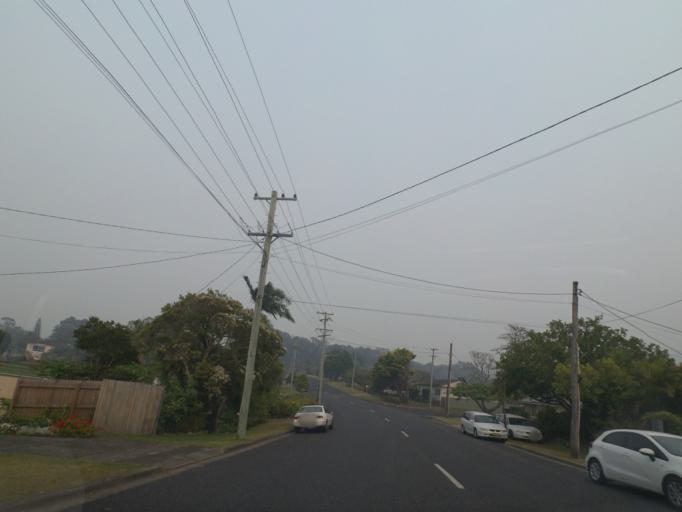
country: AU
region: New South Wales
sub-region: Coffs Harbour
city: Coffs Harbour
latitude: -30.2853
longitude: 153.1057
